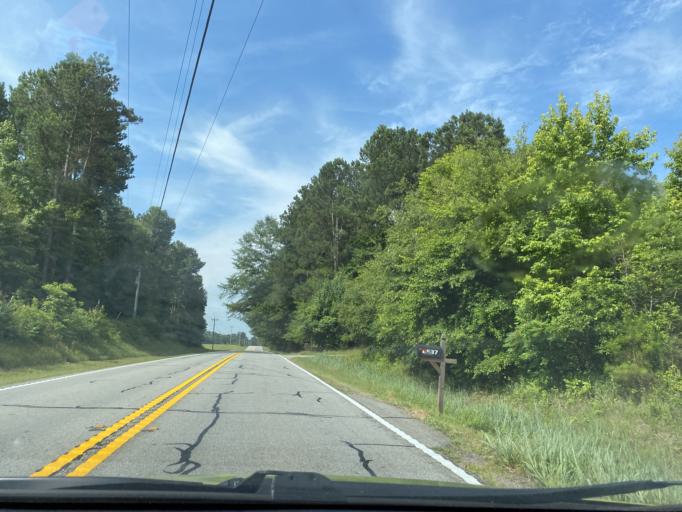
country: US
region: Georgia
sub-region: Coweta County
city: East Newnan
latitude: 33.2693
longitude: -84.7163
